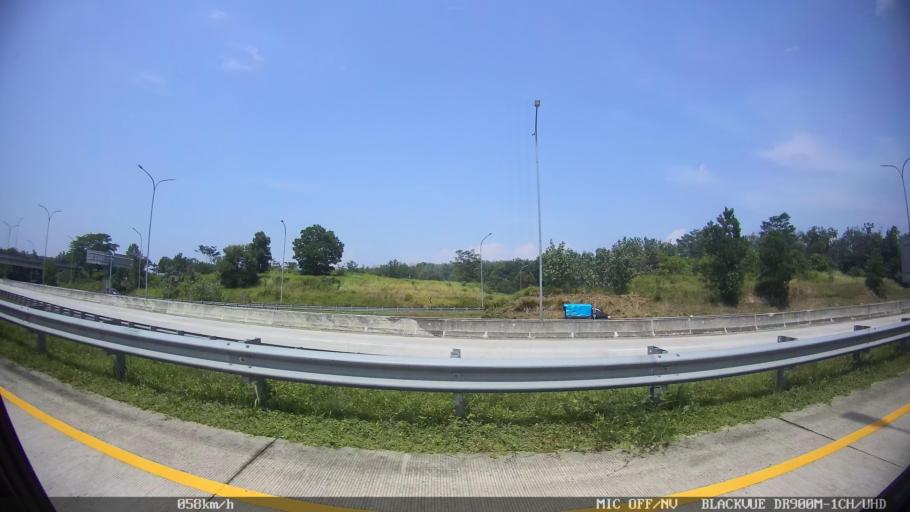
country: ID
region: Lampung
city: Kedaton
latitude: -5.3647
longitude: 105.3260
